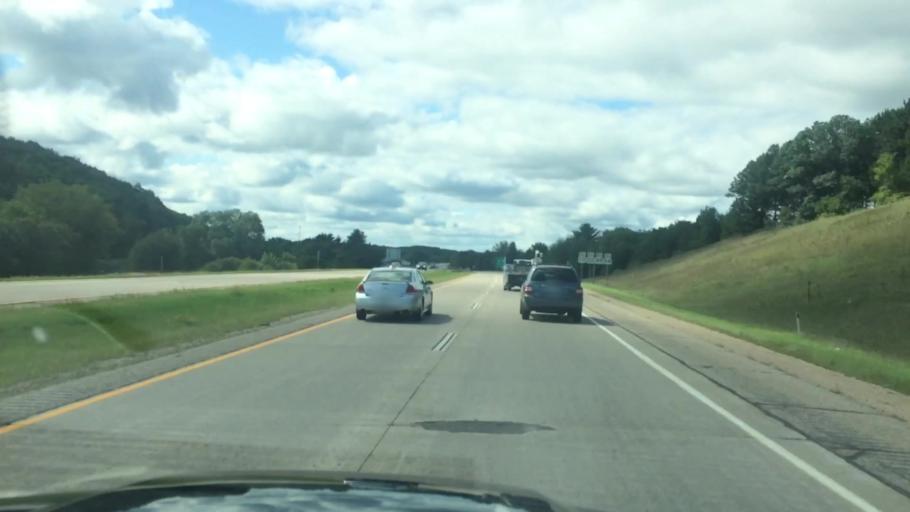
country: US
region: Wisconsin
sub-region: Waupaca County
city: Waupaca
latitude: 44.3406
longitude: -89.0760
